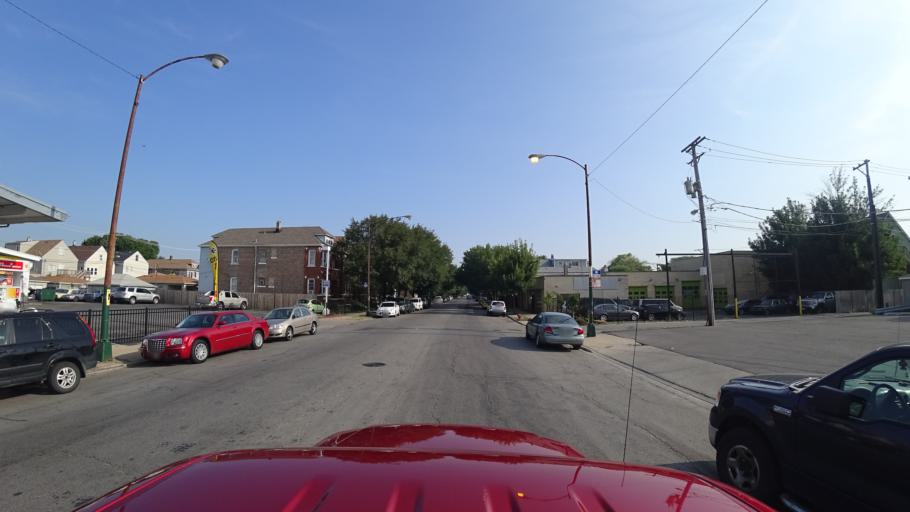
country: US
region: Illinois
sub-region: Cook County
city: Chicago
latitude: 41.8085
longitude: -87.6942
